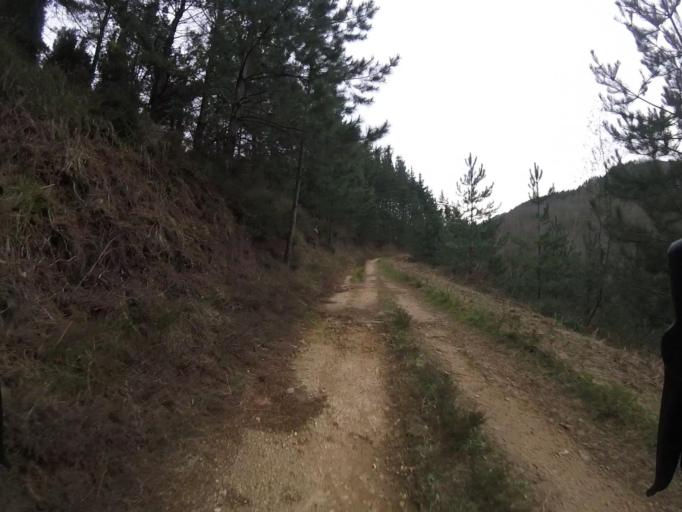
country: ES
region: Navarre
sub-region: Provincia de Navarra
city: Bera
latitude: 43.2900
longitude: -1.7343
